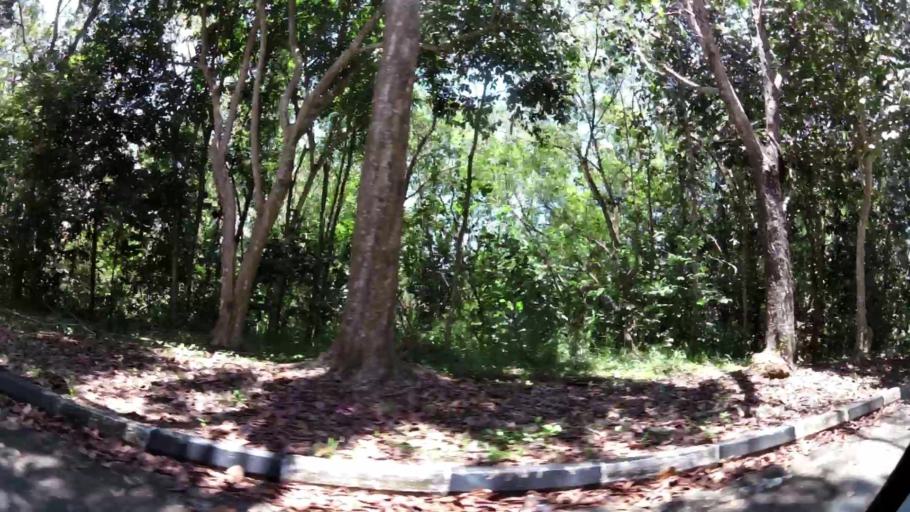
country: BN
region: Brunei and Muara
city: Bandar Seri Begawan
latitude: 4.9232
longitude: 114.9626
